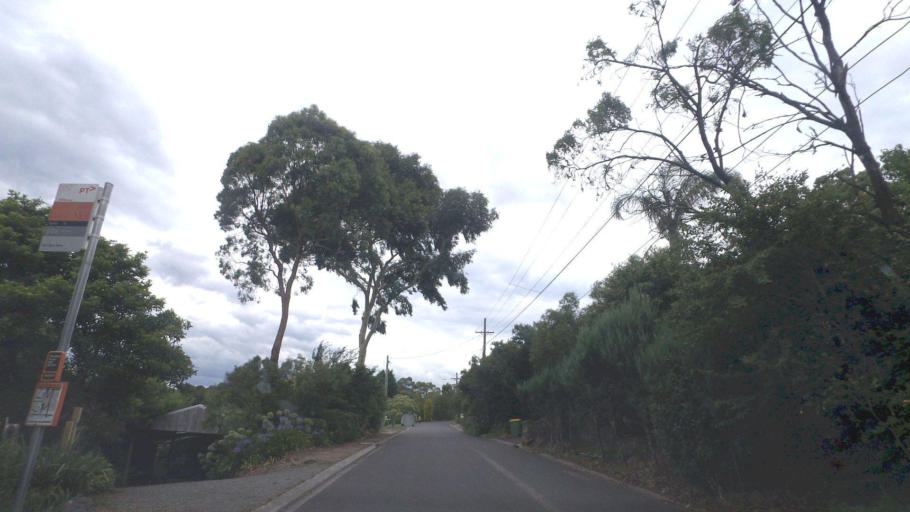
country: AU
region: Victoria
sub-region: Yarra Ranges
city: Lilydale
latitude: -37.7574
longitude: 145.3674
